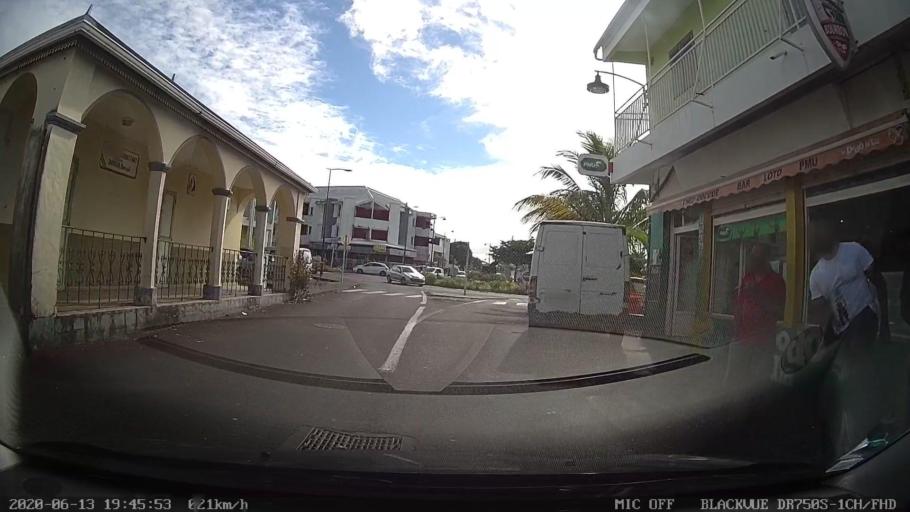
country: RE
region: Reunion
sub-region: Reunion
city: Bras-Panon
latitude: -20.9957
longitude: 55.6772
